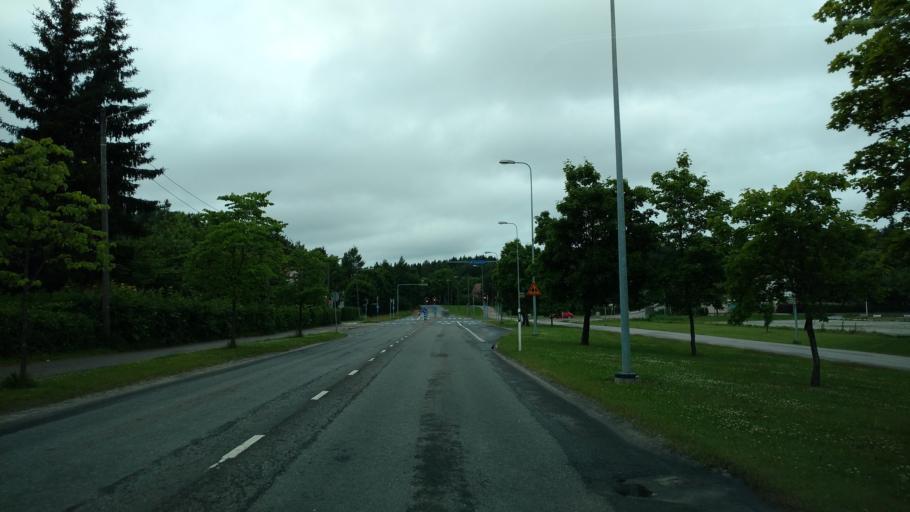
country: FI
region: Varsinais-Suomi
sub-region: Salo
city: Halikko
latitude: 60.3952
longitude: 23.1042
